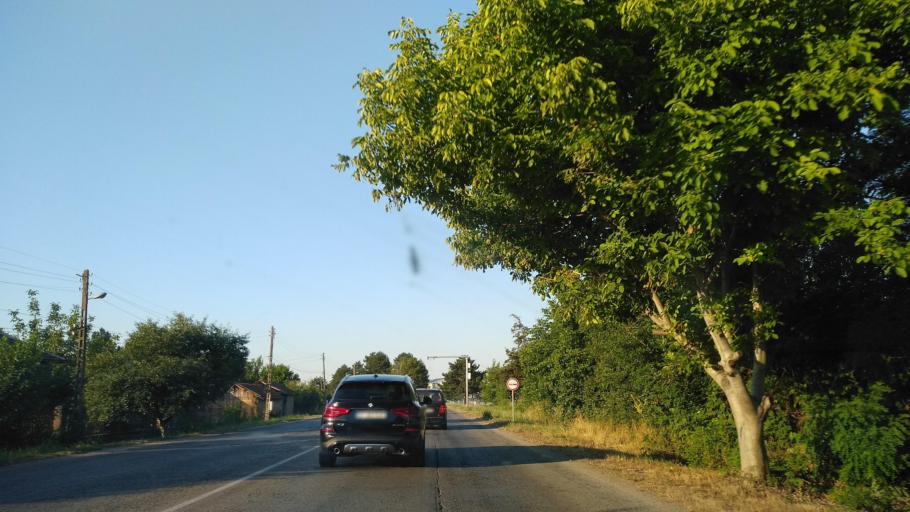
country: BG
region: Veliko Turnovo
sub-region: Obshtina Polski Trumbesh
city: Polski Trumbesh
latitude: 43.2970
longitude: 25.6415
